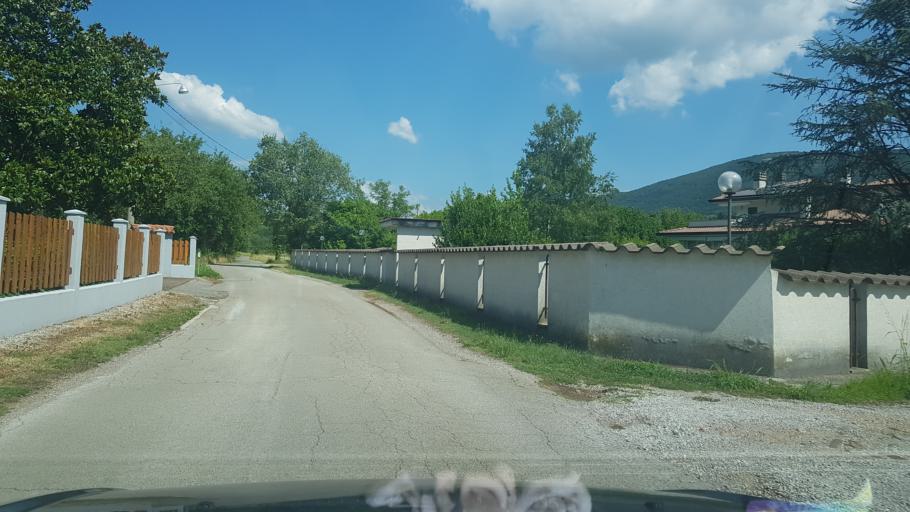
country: IT
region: Friuli Venezia Giulia
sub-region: Provincia di Gorizia
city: Gorizia
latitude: 45.9593
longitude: 13.6243
